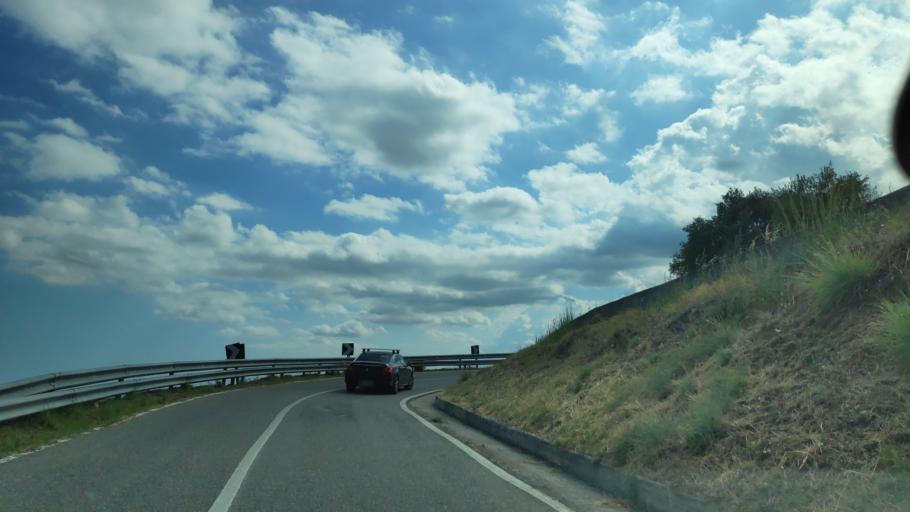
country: IT
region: Calabria
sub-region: Provincia di Catanzaro
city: Santa Caterina dello Ionio
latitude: 38.5259
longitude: 16.5341
